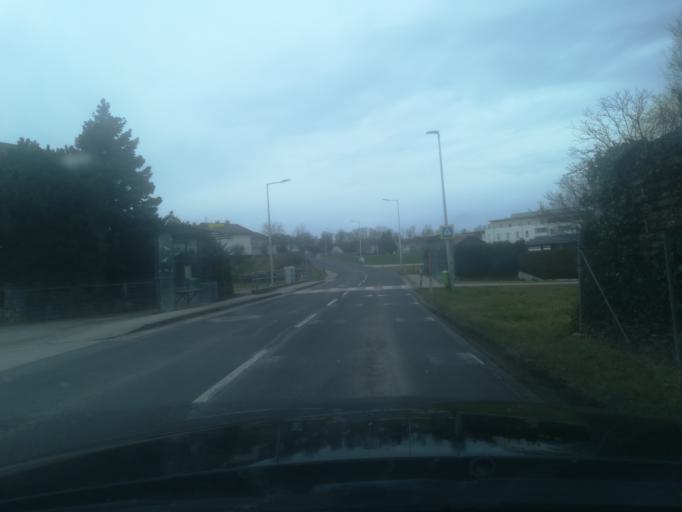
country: AT
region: Upper Austria
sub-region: Wels-Land
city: Lambach
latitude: 48.0935
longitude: 13.8988
